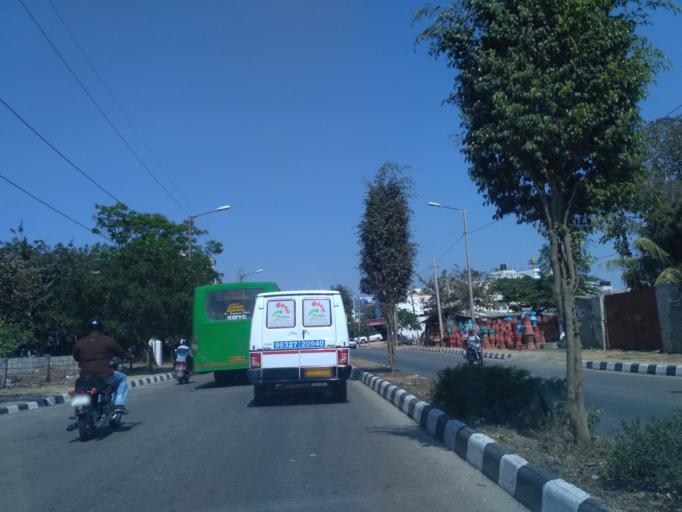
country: IN
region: Karnataka
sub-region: Bangalore Urban
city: Yelahanka
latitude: 13.0831
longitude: 77.5508
